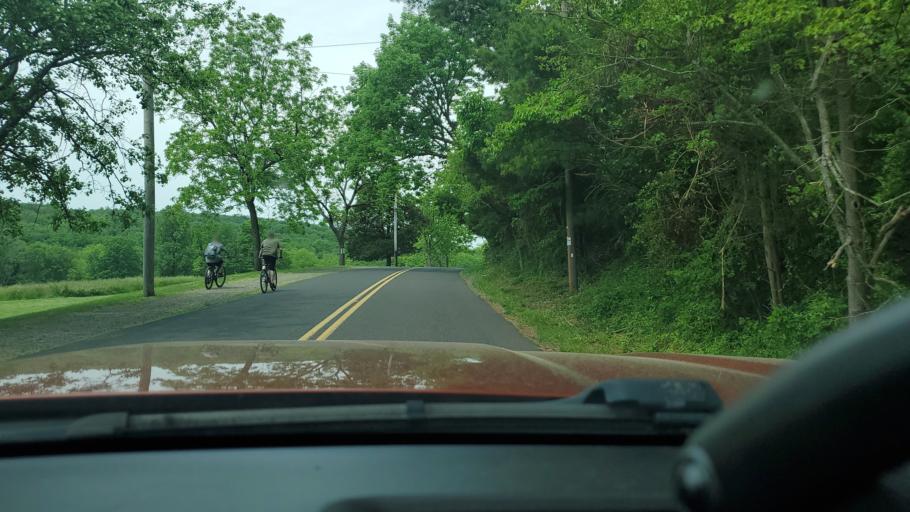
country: US
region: Pennsylvania
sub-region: Montgomery County
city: Red Hill
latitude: 40.3366
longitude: -75.4861
